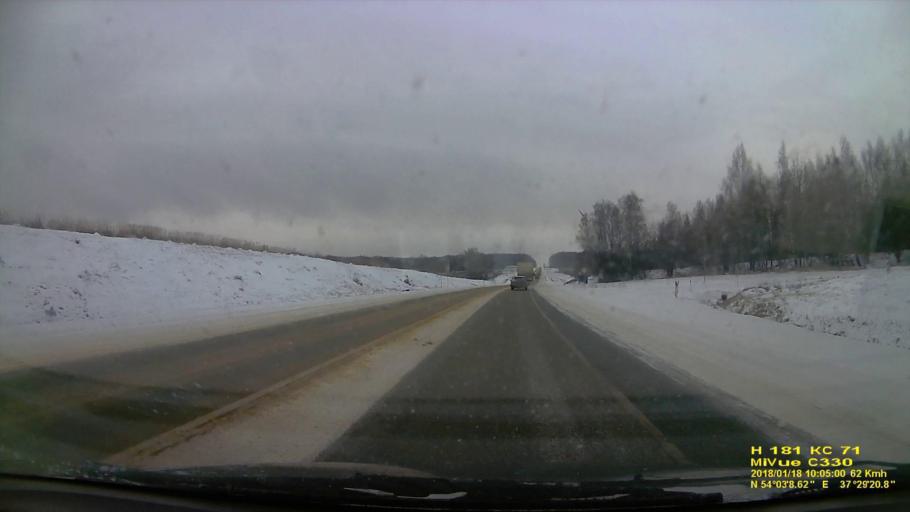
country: RU
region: Tula
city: Pervomayskiy
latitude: 54.0521
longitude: 37.4891
